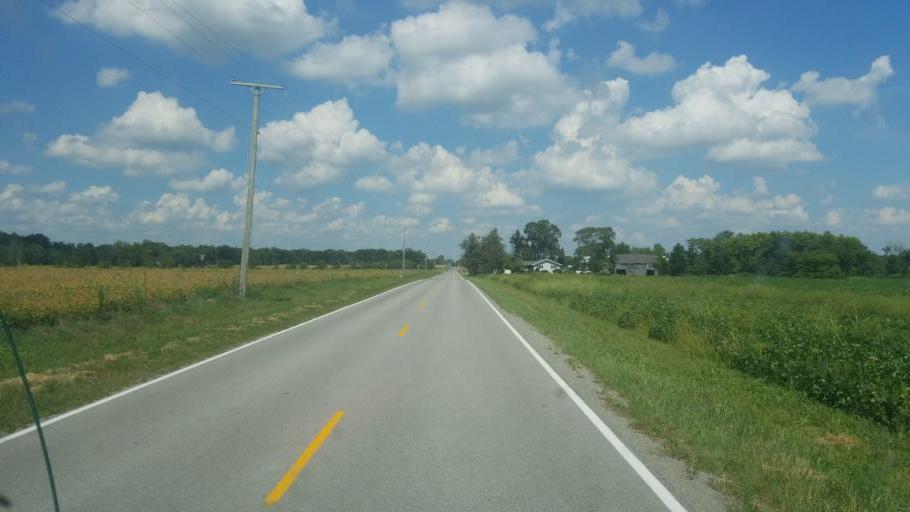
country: US
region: Ohio
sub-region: Hancock County
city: Arlington
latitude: 40.8855
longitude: -83.7271
